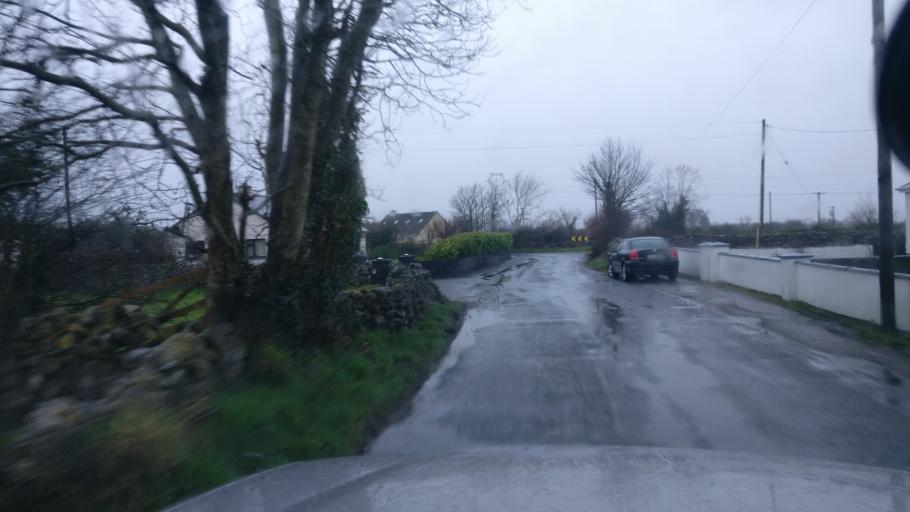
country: IE
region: Connaught
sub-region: County Galway
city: Loughrea
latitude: 53.1995
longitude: -8.5096
